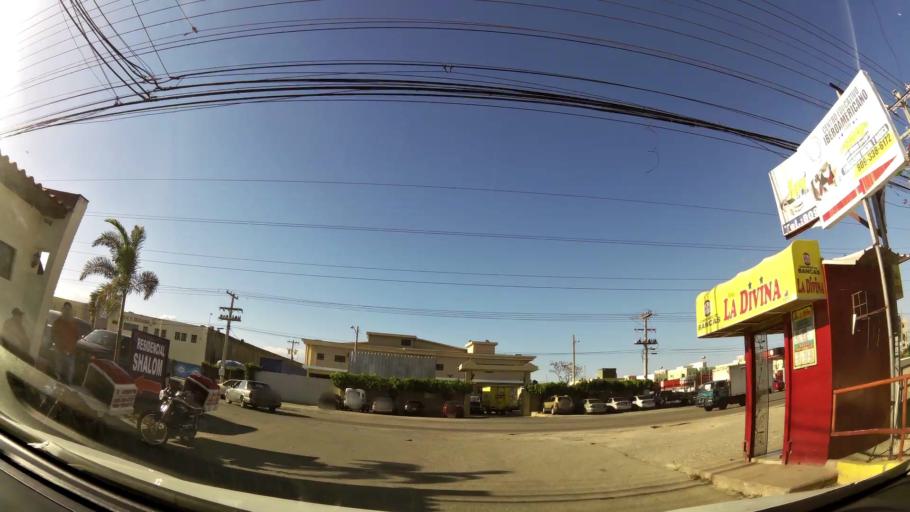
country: DO
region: Santo Domingo
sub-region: Santo Domingo
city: Santo Domingo Este
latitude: 18.4922
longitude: -69.8138
